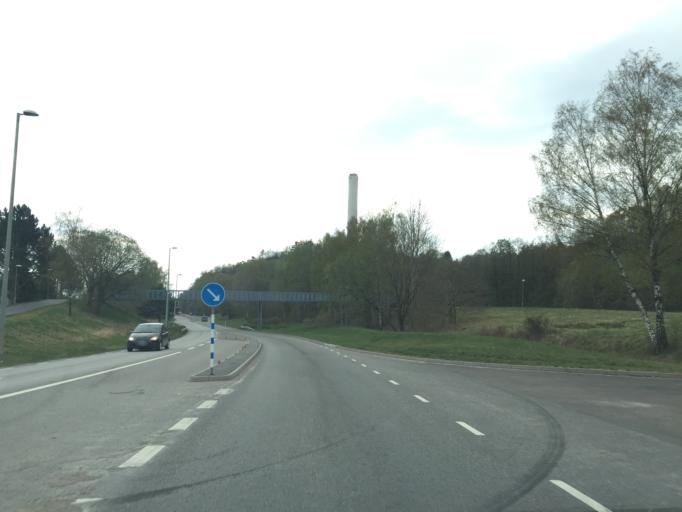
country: SE
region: Vaestra Goetaland
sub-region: Goteborg
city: Loevgaerdet
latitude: 57.8031
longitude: 12.0426
